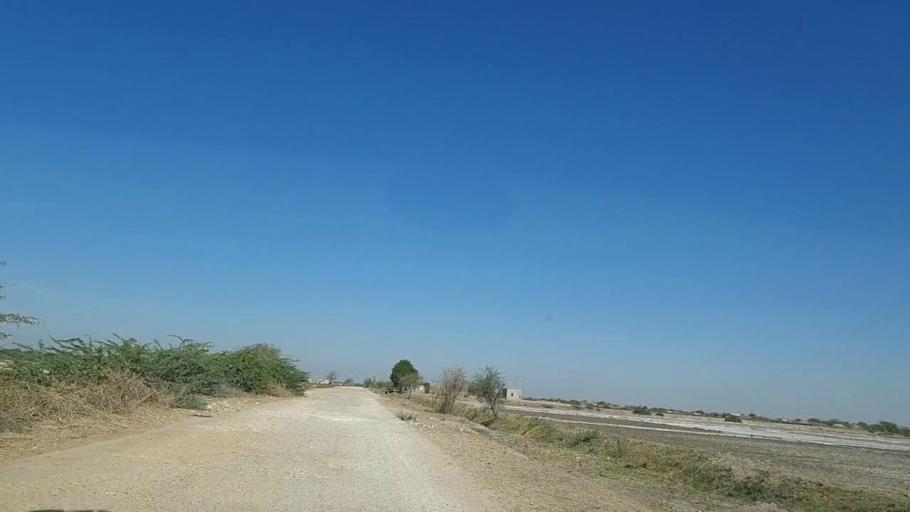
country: PK
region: Sindh
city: Dhoro Naro
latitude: 25.4803
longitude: 69.5272
